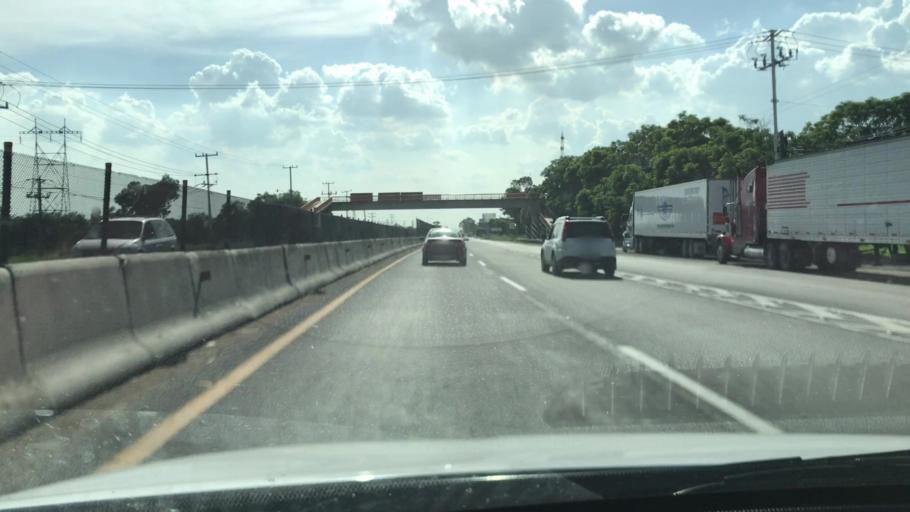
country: MX
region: Guanajuato
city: Villagran
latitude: 20.5084
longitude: -100.9964
